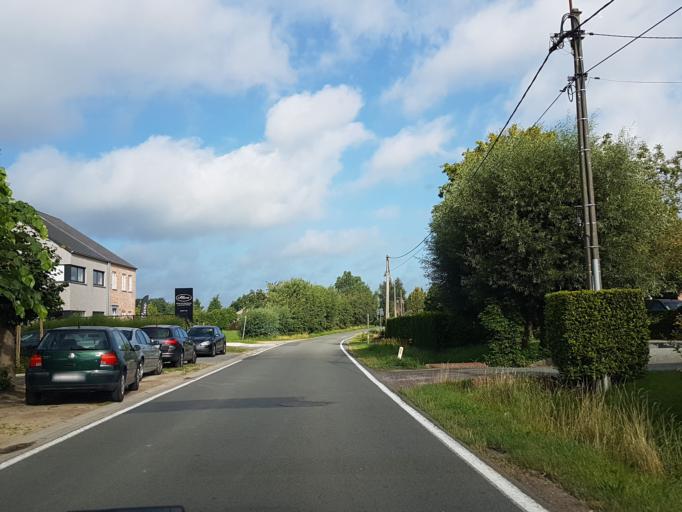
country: BE
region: Flanders
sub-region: Provincie Oost-Vlaanderen
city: Sint-Martens-Latem
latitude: 51.0568
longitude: 3.6438
